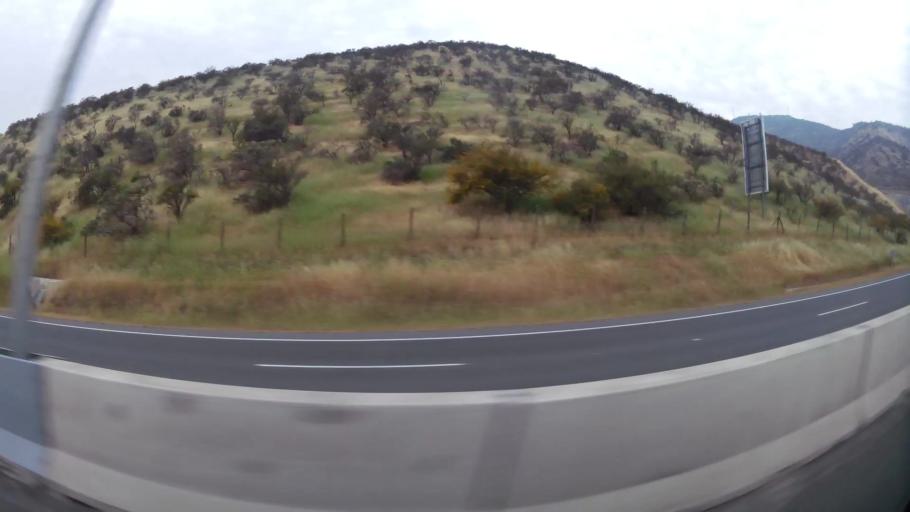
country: CL
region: Santiago Metropolitan
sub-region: Provincia de Chacabuco
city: Chicureo Abajo
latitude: -33.3307
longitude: -70.6281
